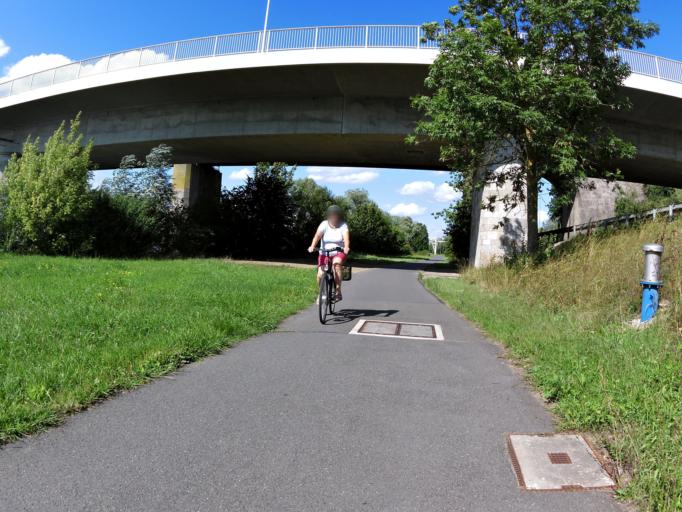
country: DE
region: Bavaria
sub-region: Regierungsbezirk Unterfranken
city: Kitzingen
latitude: 49.7250
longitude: 10.1645
